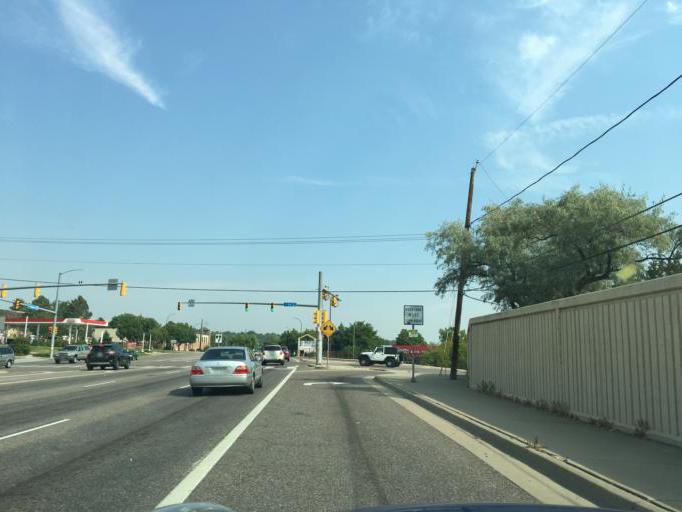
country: US
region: Colorado
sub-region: Jefferson County
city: Arvada
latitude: 39.8123
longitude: -105.0800
